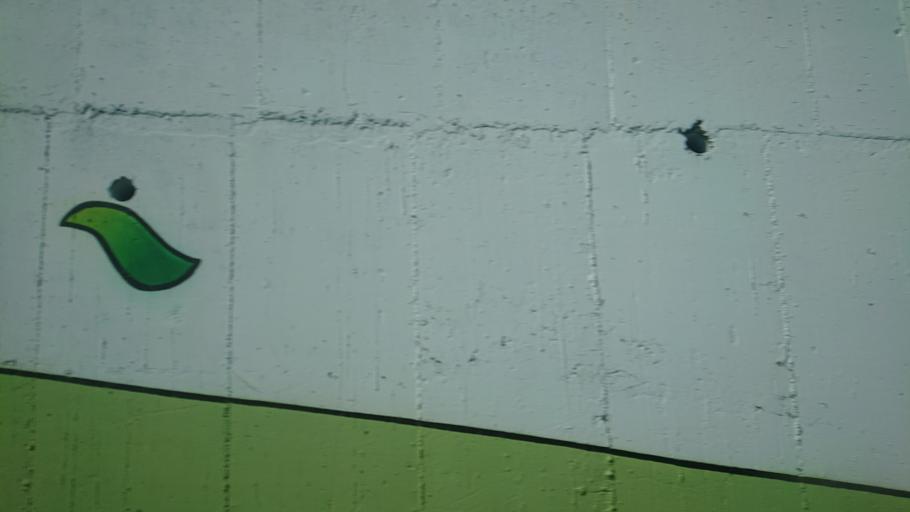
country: TW
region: Taiwan
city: Lugu
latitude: 23.7501
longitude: 120.6588
